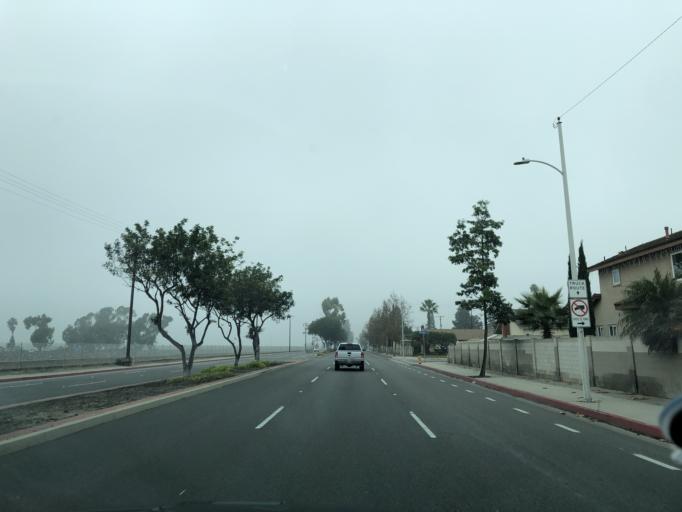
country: US
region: California
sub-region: Orange County
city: Westminster
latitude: 33.7340
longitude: -118.0415
